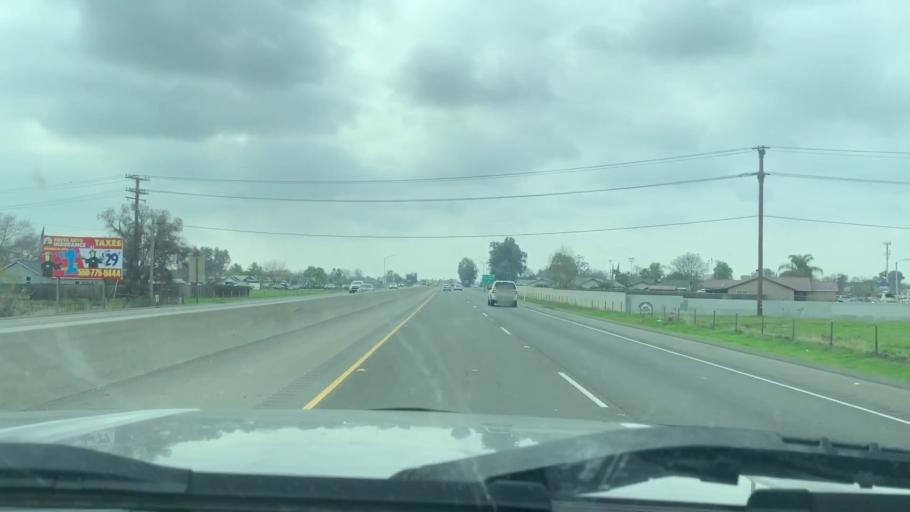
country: US
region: California
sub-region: Kings County
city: Armona
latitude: 36.3114
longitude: -119.7015
